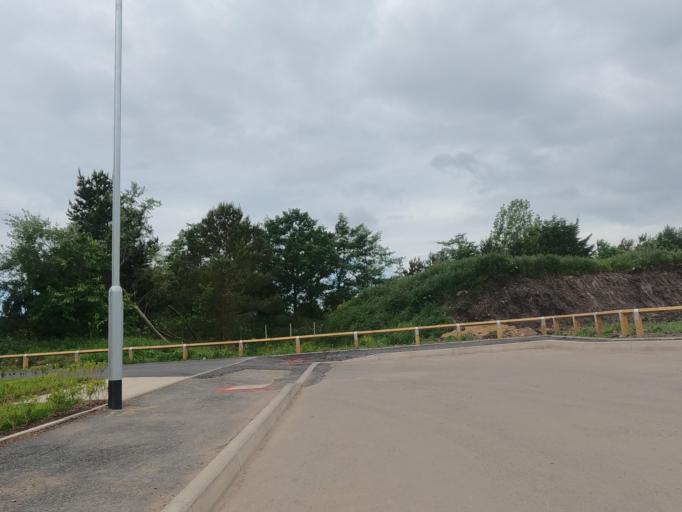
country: GB
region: England
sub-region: Northumberland
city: Blyth
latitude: 55.1115
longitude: -1.5400
